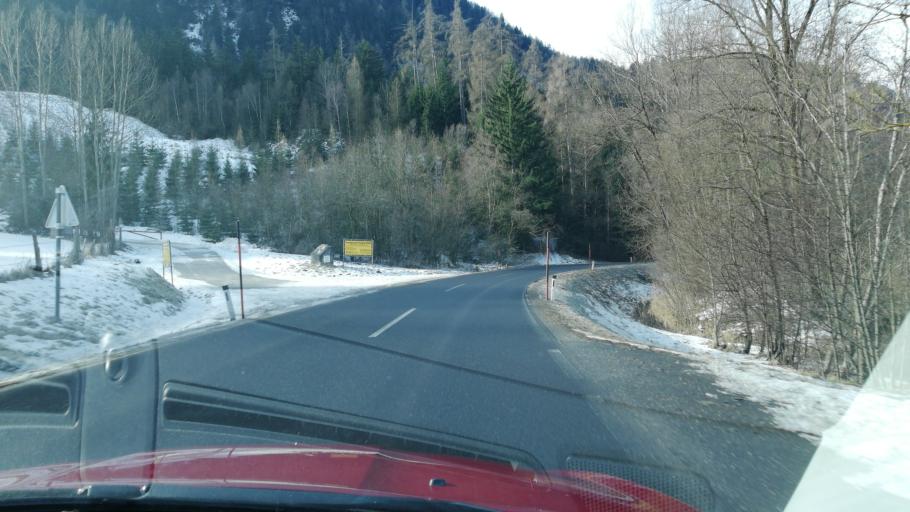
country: AT
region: Styria
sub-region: Politischer Bezirk Liezen
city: Weissenbach bei Liezen
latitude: 47.5423
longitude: 14.1874
